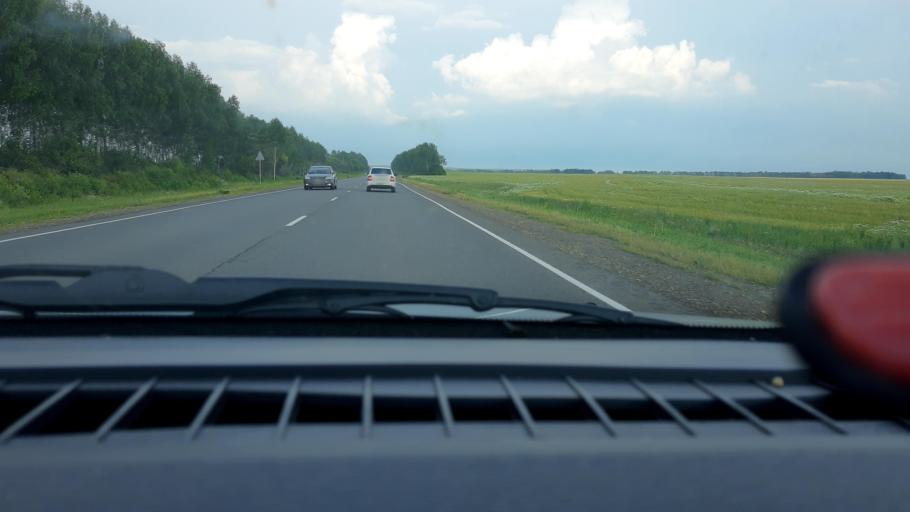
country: RU
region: Nizjnij Novgorod
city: Shatki
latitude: 55.2437
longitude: 44.0180
